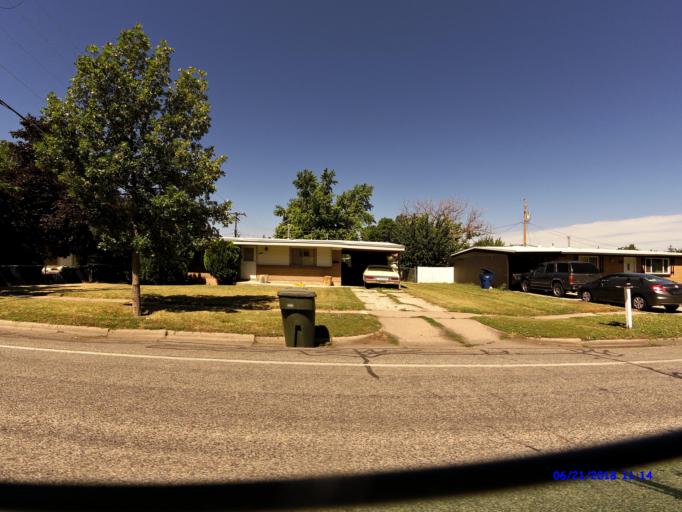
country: US
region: Utah
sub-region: Weber County
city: Harrisville
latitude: 41.2760
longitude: -111.9591
